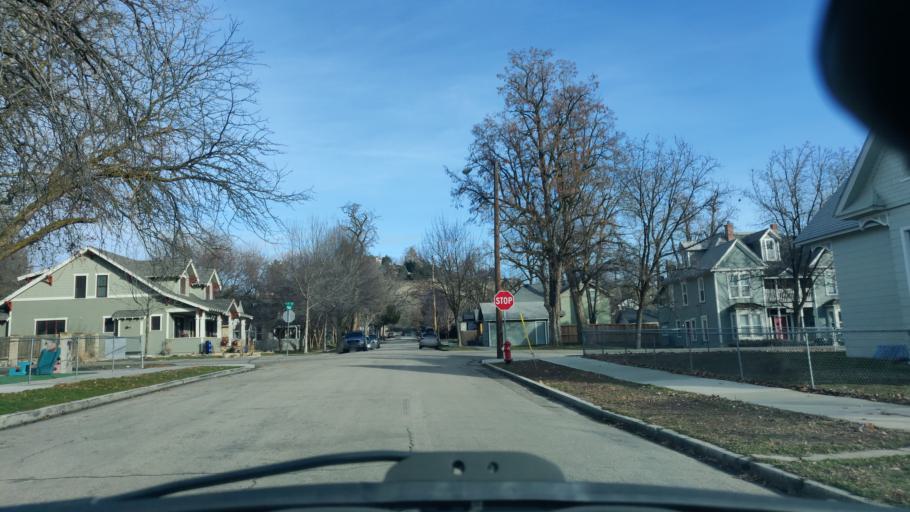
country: US
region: Idaho
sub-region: Ada County
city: Boise
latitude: 43.6302
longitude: -116.1992
